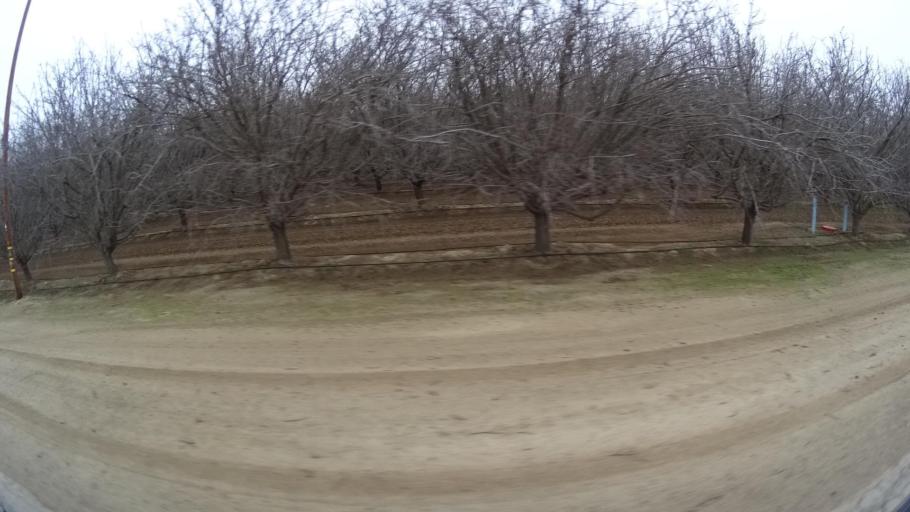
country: US
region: California
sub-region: Kern County
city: Wasco
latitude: 35.5688
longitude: -119.4918
